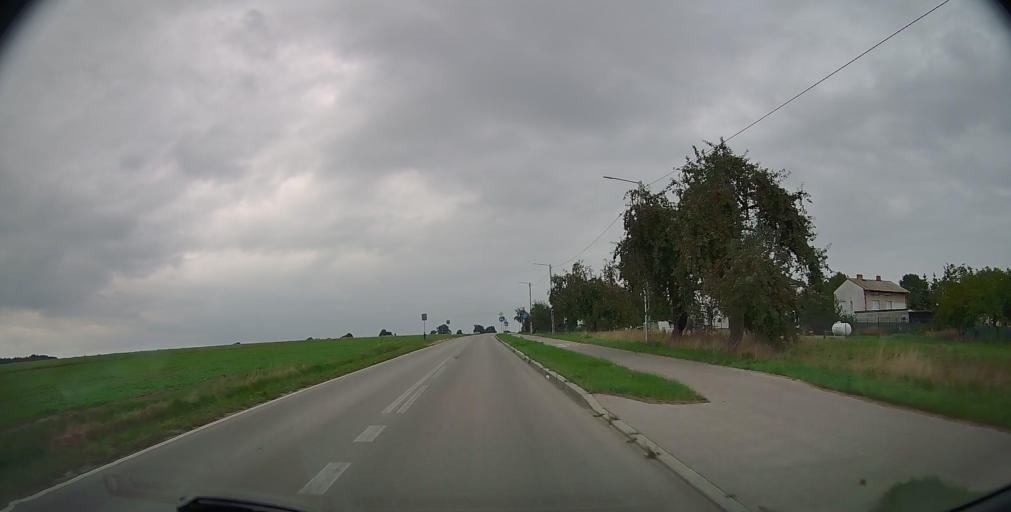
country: PL
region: Masovian Voivodeship
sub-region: Powiat radomski
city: Zakrzew
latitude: 51.4369
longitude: 21.0519
